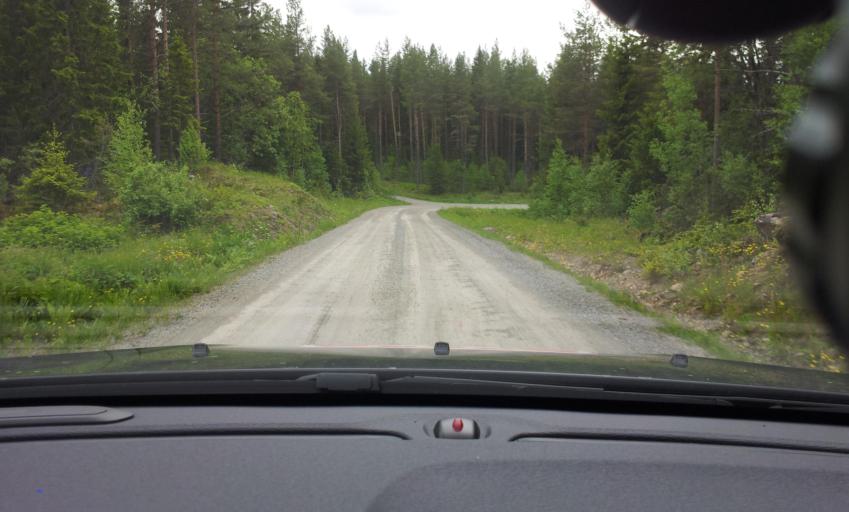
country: SE
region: Jaemtland
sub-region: OEstersunds Kommun
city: Brunflo
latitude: 62.9810
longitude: 14.7036
